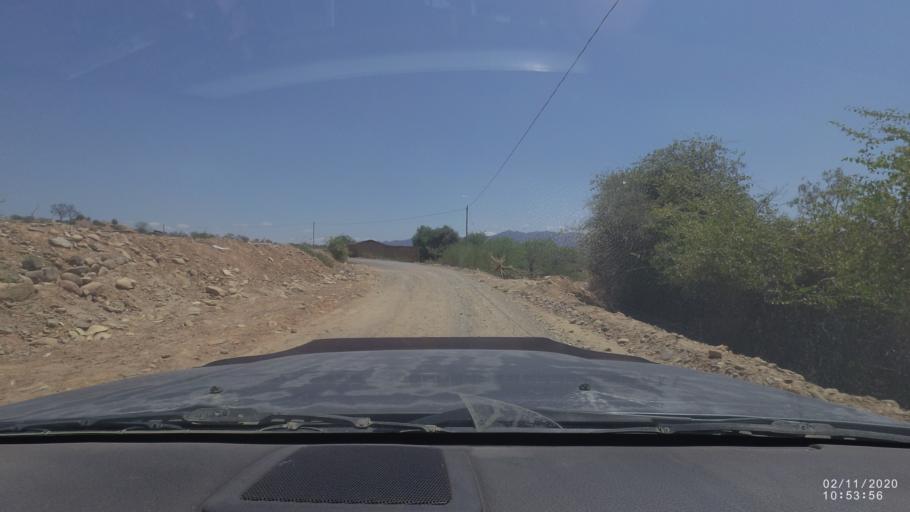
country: BO
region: Cochabamba
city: Aiquile
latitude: -18.1751
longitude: -64.8696
